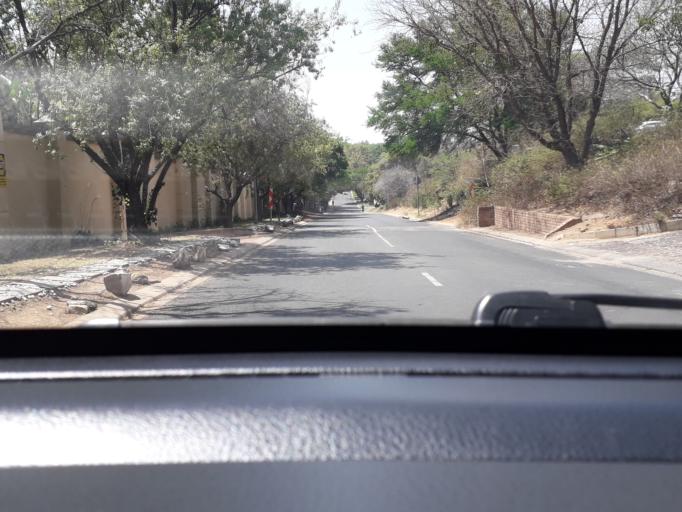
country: ZA
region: Gauteng
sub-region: City of Johannesburg Metropolitan Municipality
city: Diepsloot
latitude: -26.0446
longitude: 28.0276
